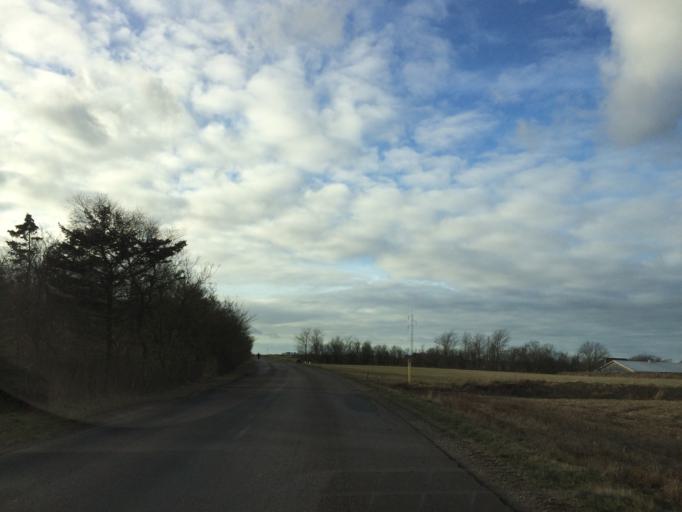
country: DK
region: Central Jutland
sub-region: Lemvig Kommune
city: Lemvig
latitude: 56.5213
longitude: 8.3493
